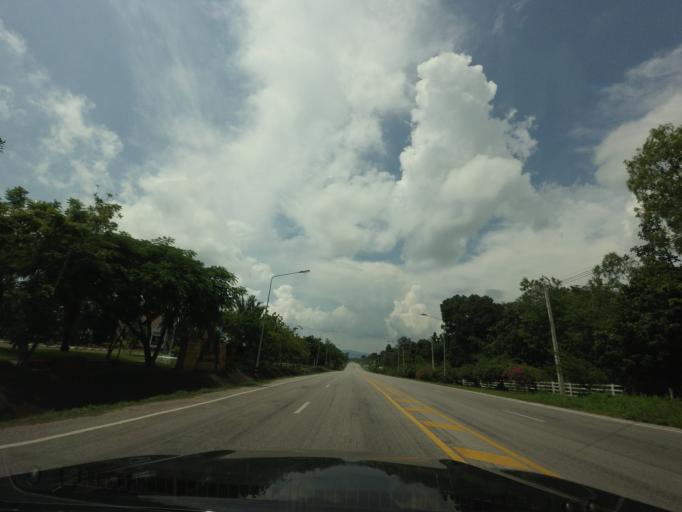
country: TH
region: Khon Kaen
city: Phu Wiang
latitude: 16.6786
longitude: 102.3406
